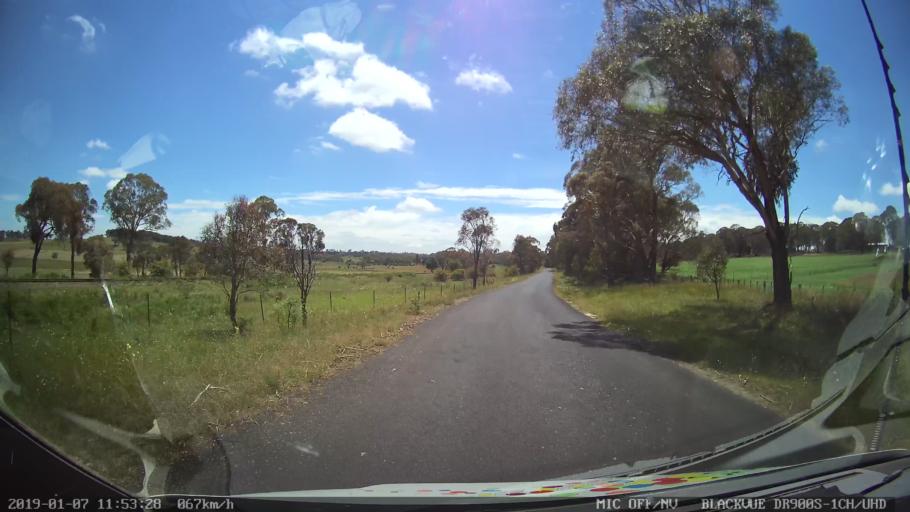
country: AU
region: New South Wales
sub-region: Guyra
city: Guyra
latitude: -30.3039
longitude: 151.6577
